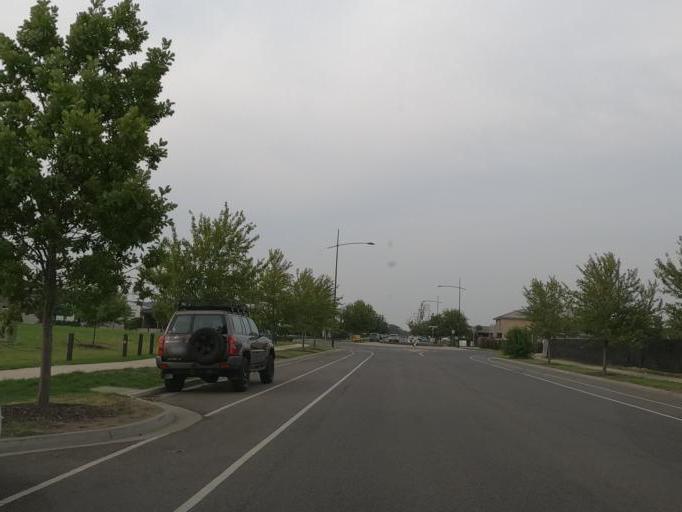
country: AU
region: Victoria
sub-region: Hume
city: Greenvale
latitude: -37.6229
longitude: 144.8786
